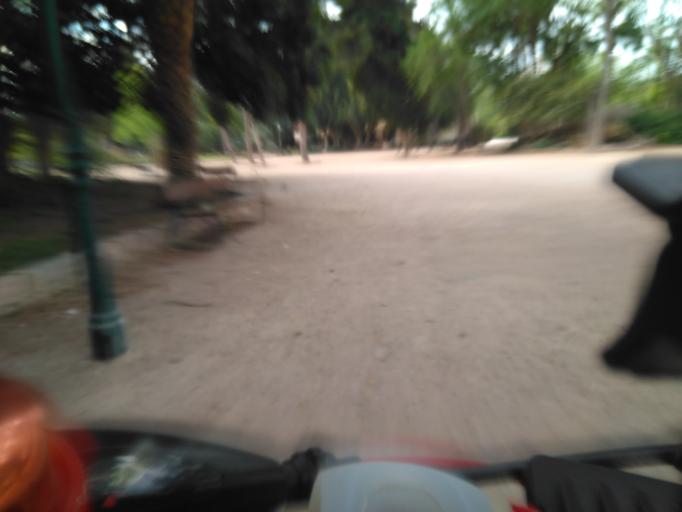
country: ES
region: Valencia
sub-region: Provincia de Valencia
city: Valencia
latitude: 39.4815
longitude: -0.3677
